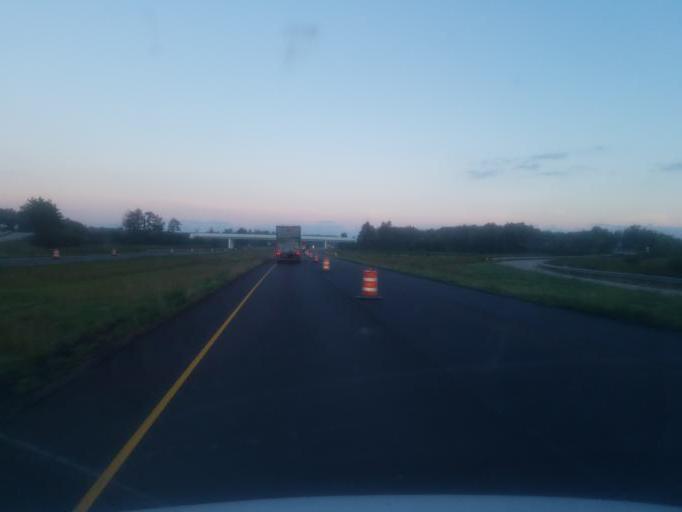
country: US
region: Ohio
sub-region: Ashtabula County
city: Ashtabula
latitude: 41.8065
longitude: -80.7561
